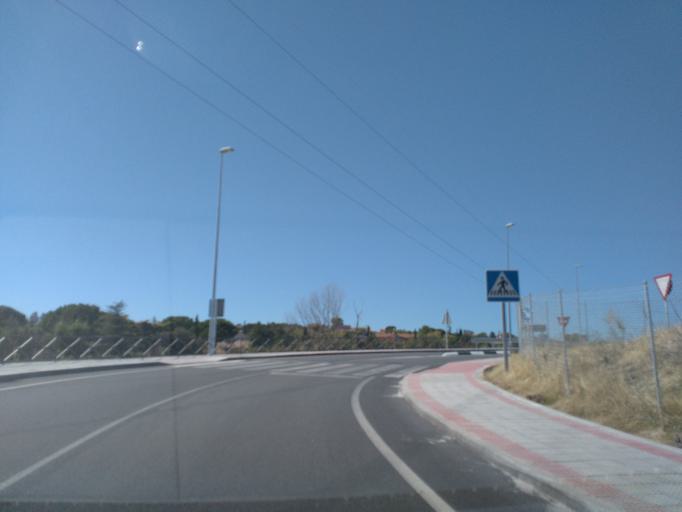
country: ES
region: Madrid
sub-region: Provincia de Madrid
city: Villanueva del Pardillo
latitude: 40.4845
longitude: -3.9398
